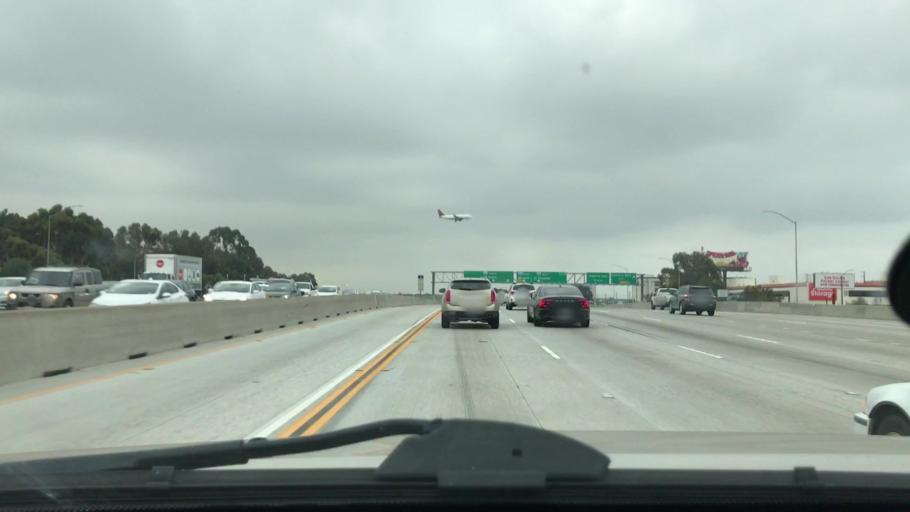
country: US
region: California
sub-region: Los Angeles County
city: Lennox
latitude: 33.9462
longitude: -118.3685
